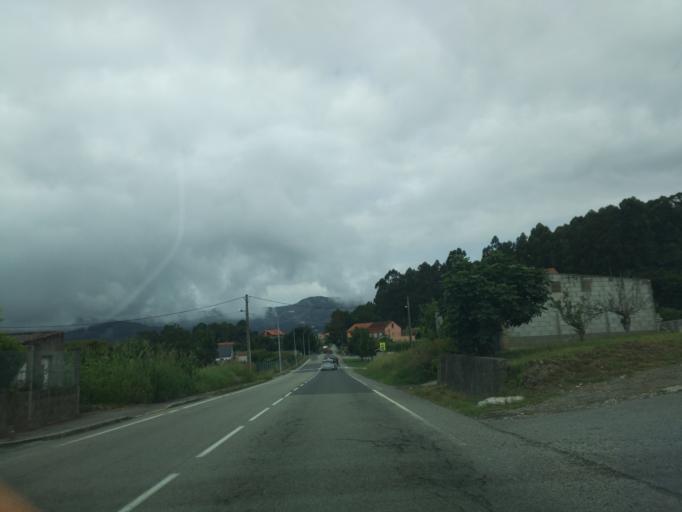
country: ES
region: Galicia
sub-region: Provincia da Coruna
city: Boiro
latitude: 42.6422
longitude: -8.8671
